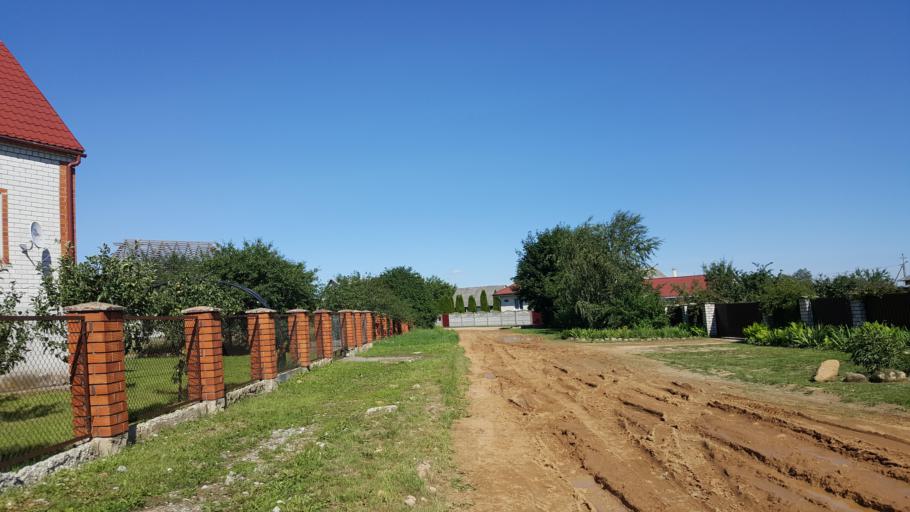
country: BY
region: Brest
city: Charnawchytsy
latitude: 52.2052
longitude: 23.7380
